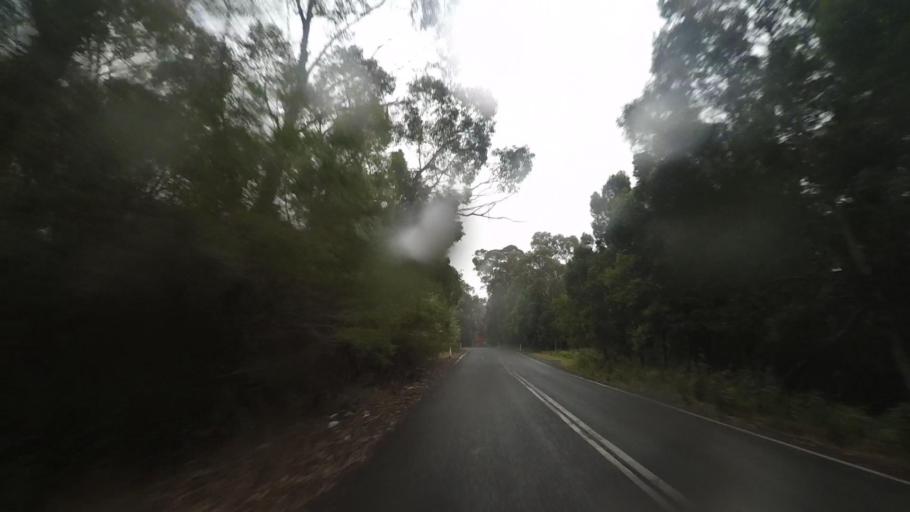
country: AU
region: New South Wales
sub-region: Wollongong
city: Mount Keira
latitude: -34.3957
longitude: 150.8452
